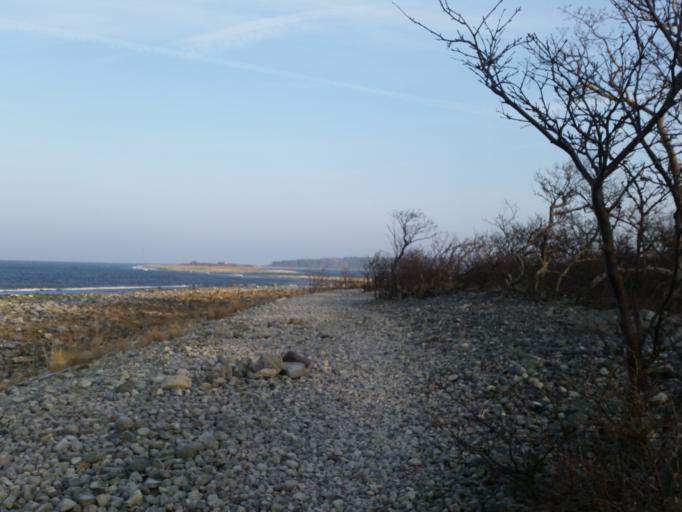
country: SE
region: Kalmar
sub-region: Vasterviks Kommun
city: Vaestervik
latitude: 57.3669
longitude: 17.0982
